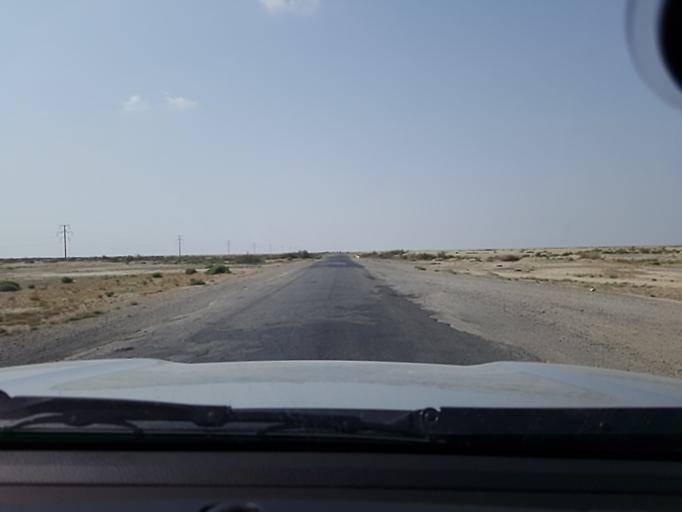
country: TM
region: Balkan
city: Gumdag
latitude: 38.8999
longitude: 54.5922
